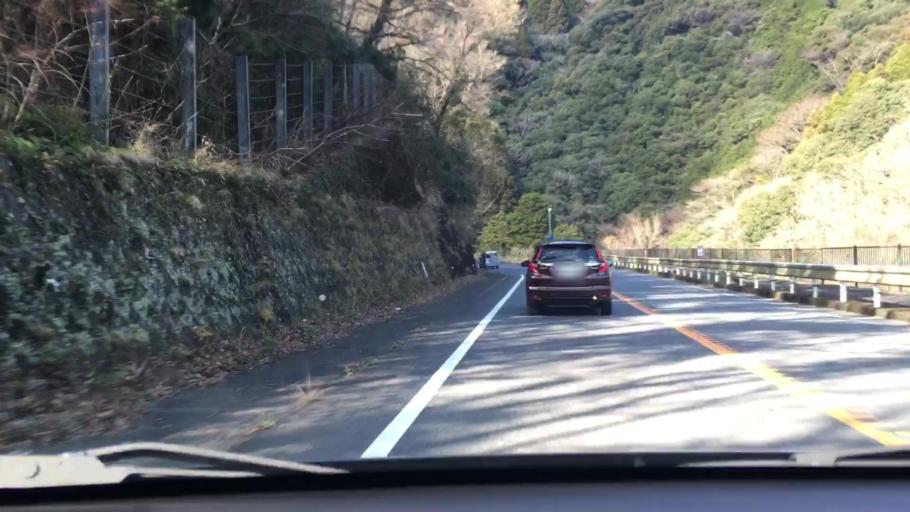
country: JP
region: Oita
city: Tsukumiura
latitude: 33.0016
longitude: 131.8037
